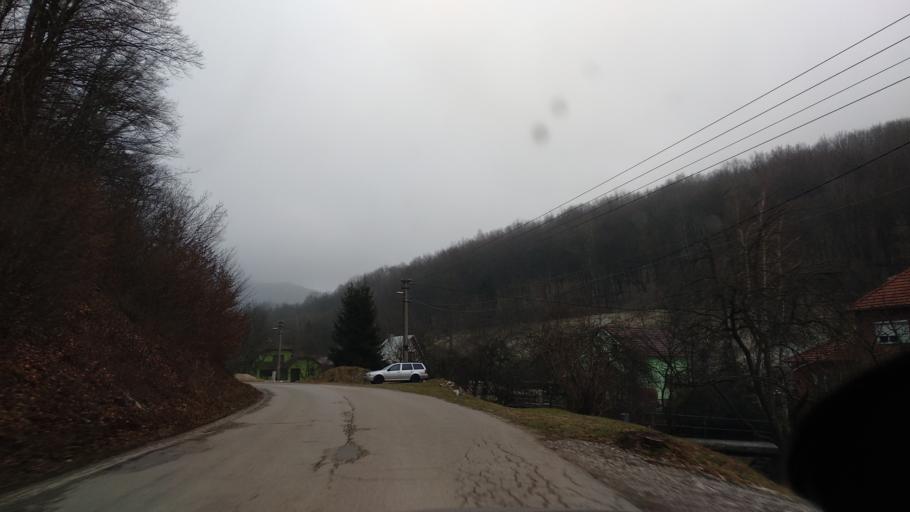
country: SK
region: Nitriansky
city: Ilava
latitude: 48.9016
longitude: 18.2719
